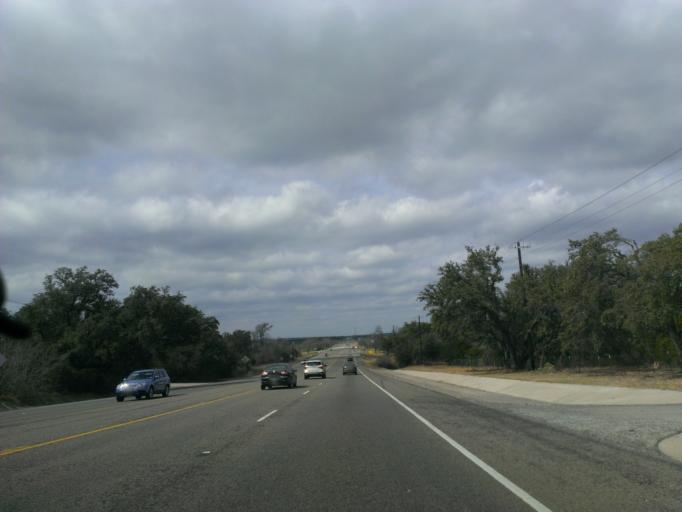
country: US
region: Texas
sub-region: Travis County
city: Briarcliff
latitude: 30.4634
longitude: -98.1628
